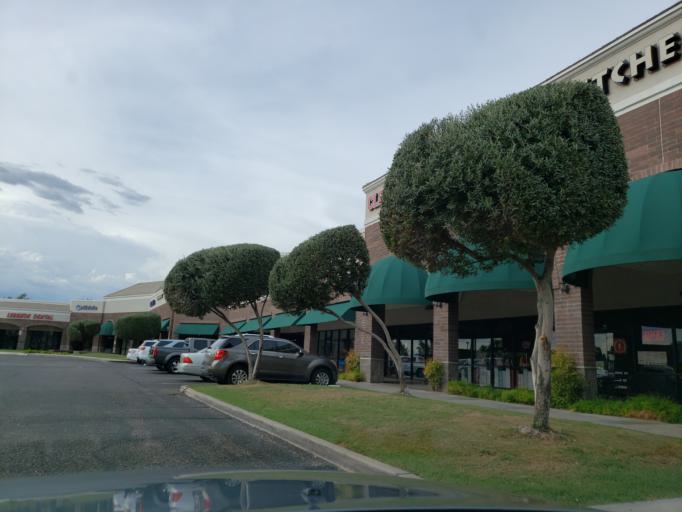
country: US
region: Arizona
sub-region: Maricopa County
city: Peoria
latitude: 33.6702
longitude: -112.2007
